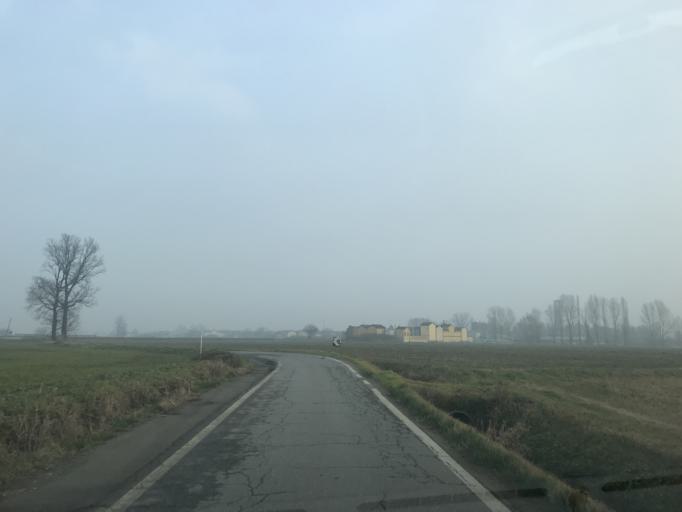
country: IT
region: Lombardy
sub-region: Provincia di Lodi
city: Villanova del Sillaro
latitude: 45.2402
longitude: 9.4743
